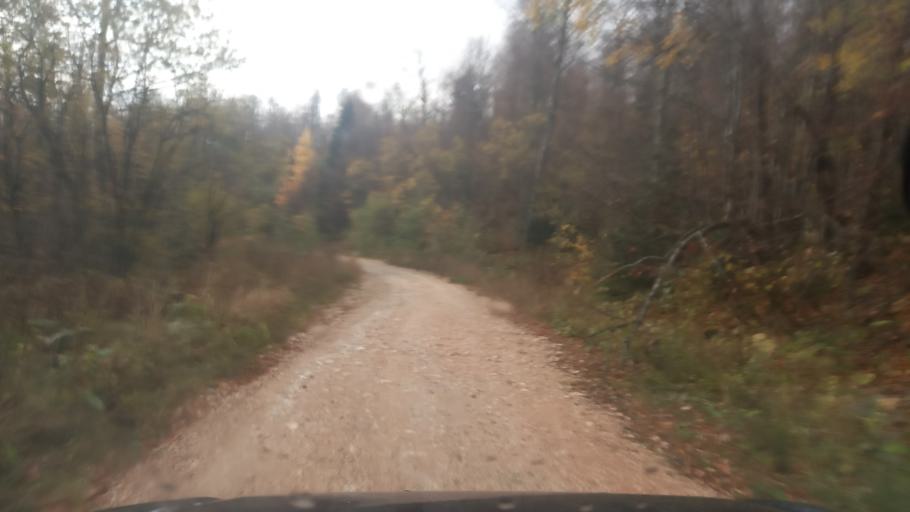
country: RU
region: Krasnodarskiy
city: Gornoye Loo
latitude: 44.0036
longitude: 39.8460
